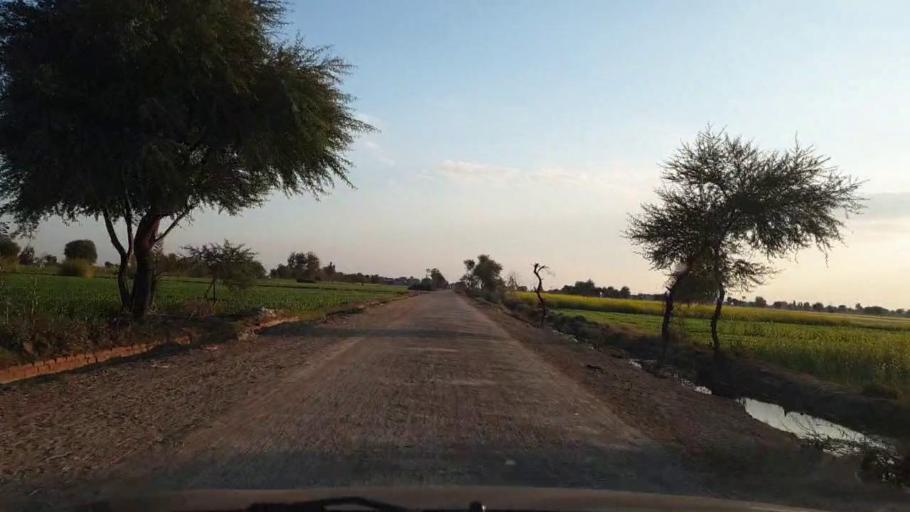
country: PK
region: Sindh
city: Sinjhoro
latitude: 26.0028
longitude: 68.8013
